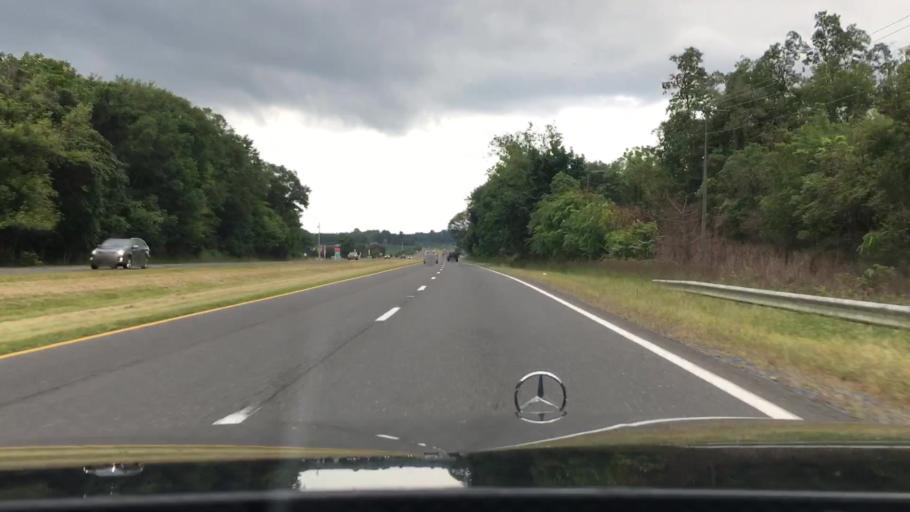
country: US
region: Virginia
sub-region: City of Winchester
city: Winchester
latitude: 39.2238
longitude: -78.1980
